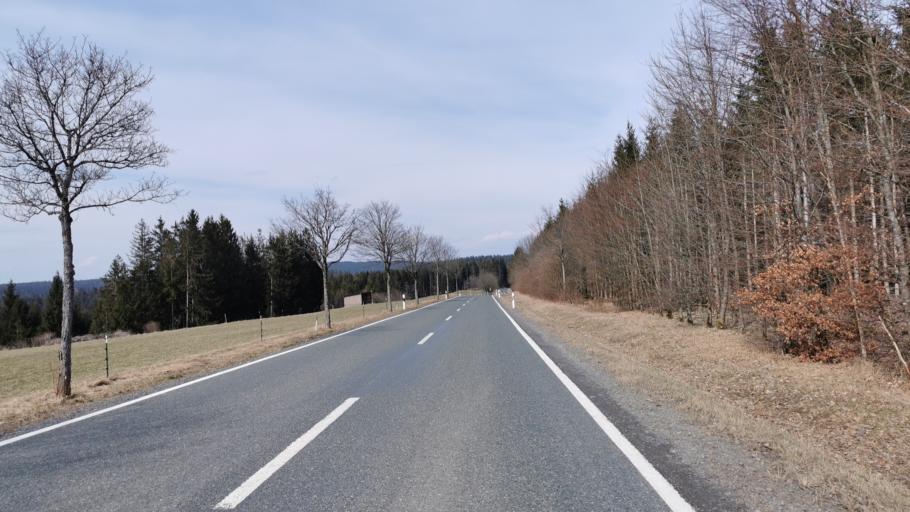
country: DE
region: Bavaria
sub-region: Upper Franconia
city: Tschirn
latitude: 50.4112
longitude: 11.4516
